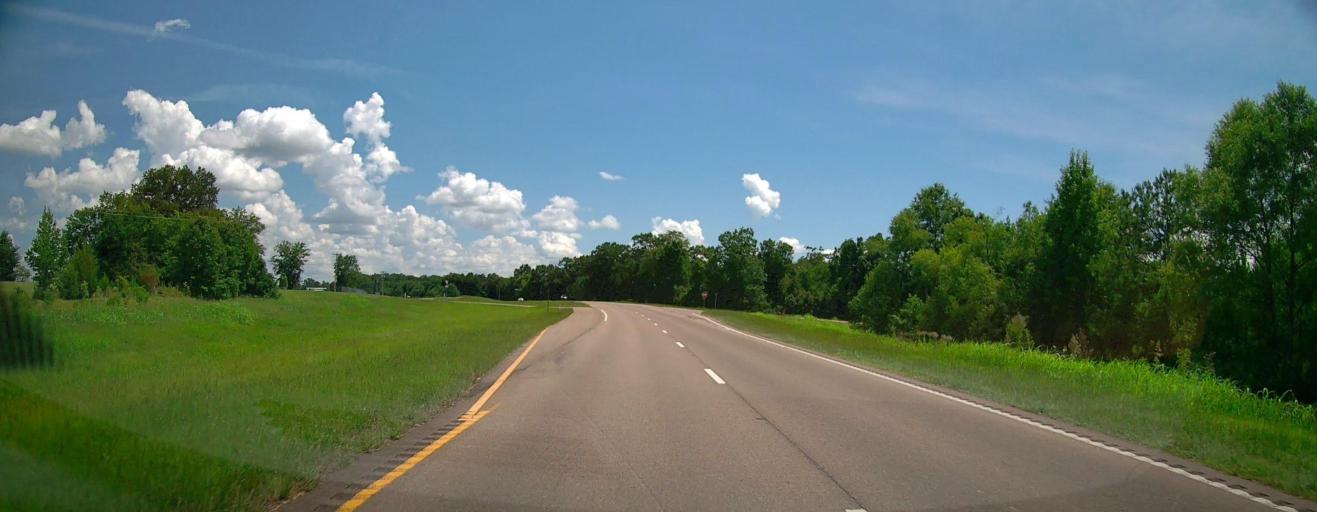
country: US
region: Mississippi
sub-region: Lee County
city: Nettleton
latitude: 33.9662
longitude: -88.6139
